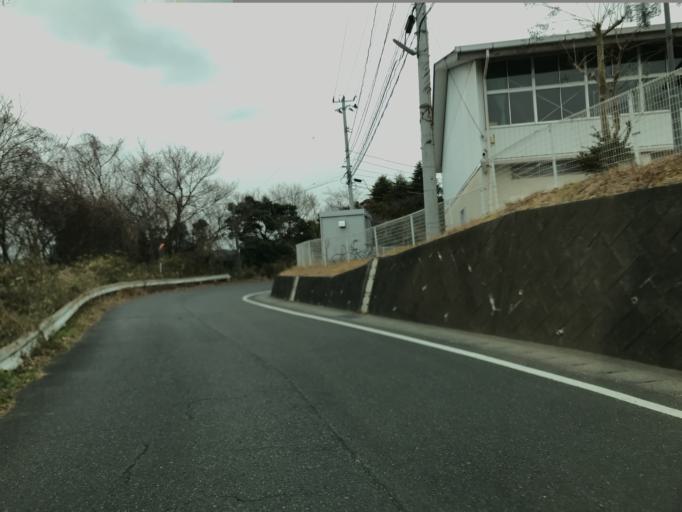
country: JP
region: Fukushima
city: Iwaki
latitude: 37.0600
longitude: 140.9062
